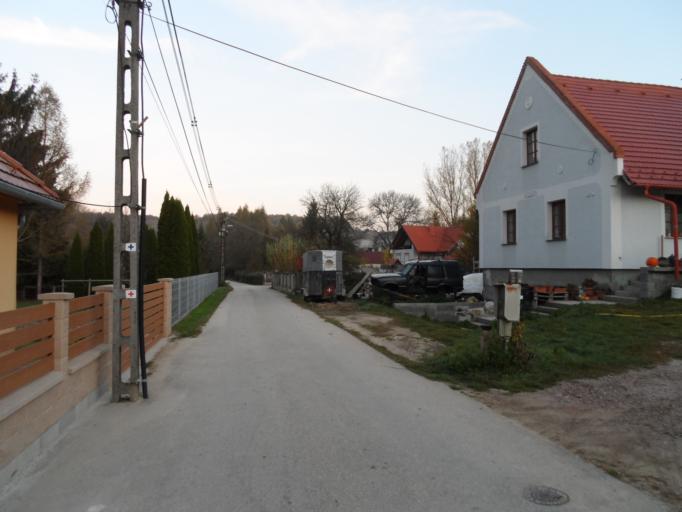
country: HU
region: Veszprem
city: Herend
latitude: 47.1814
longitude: 17.6825
